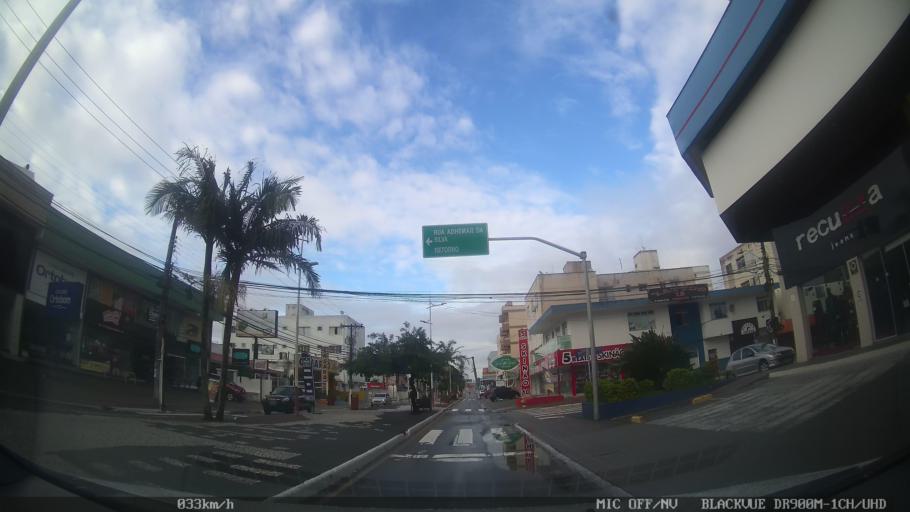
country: BR
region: Santa Catarina
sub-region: Sao Jose
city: Campinas
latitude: -27.5995
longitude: -48.6148
